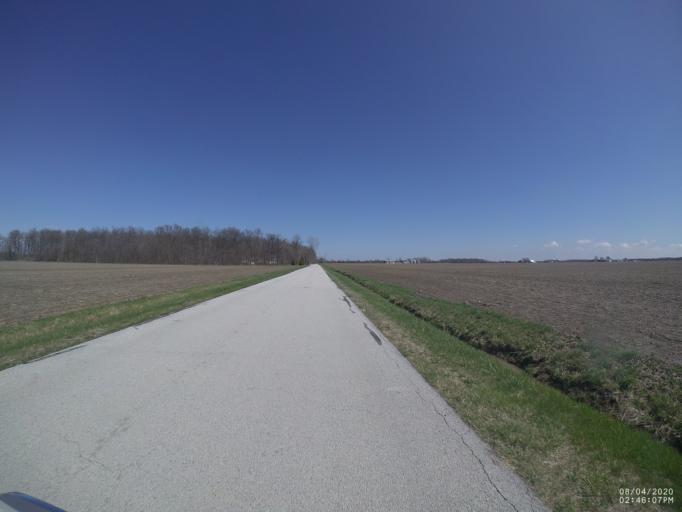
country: US
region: Ohio
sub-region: Sandusky County
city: Gibsonburg
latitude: 41.2974
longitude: -83.2843
